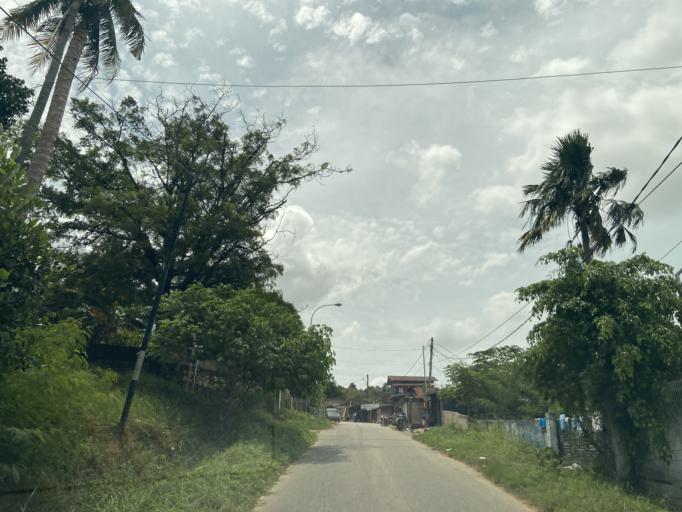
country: SG
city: Singapore
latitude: 1.1512
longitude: 104.0134
